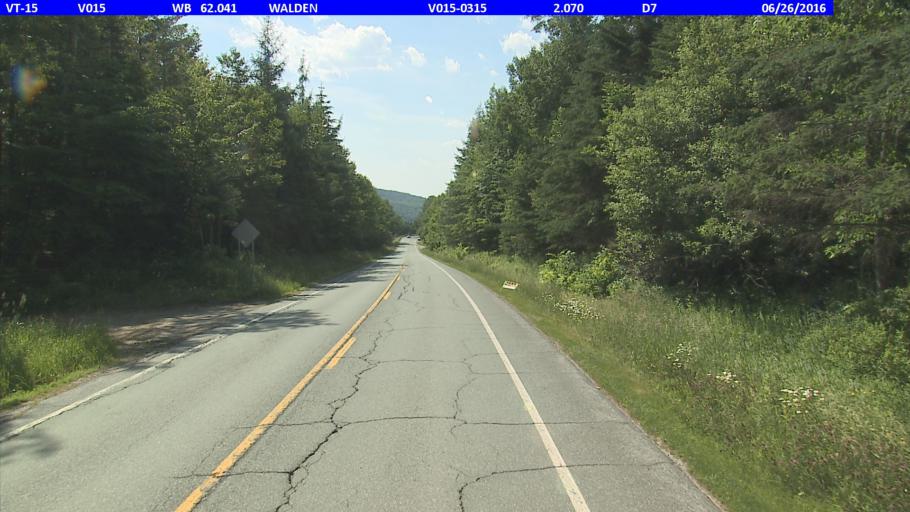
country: US
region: Vermont
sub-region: Caledonia County
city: Hardwick
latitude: 44.4678
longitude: -72.2729
